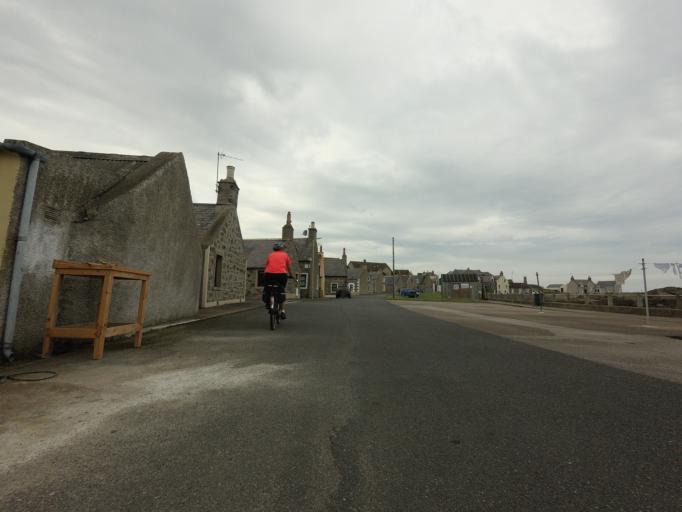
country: GB
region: Scotland
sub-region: Aberdeenshire
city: Whitehills
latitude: 57.6773
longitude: -2.5839
